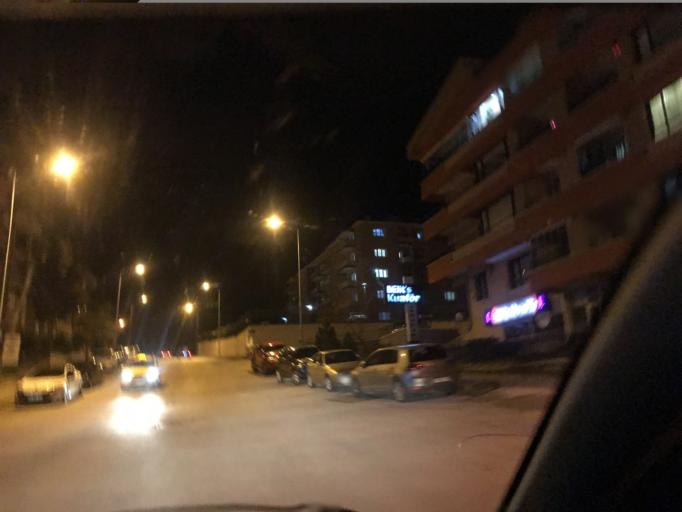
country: TR
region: Ankara
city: Cankaya
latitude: 39.8817
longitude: 32.8742
